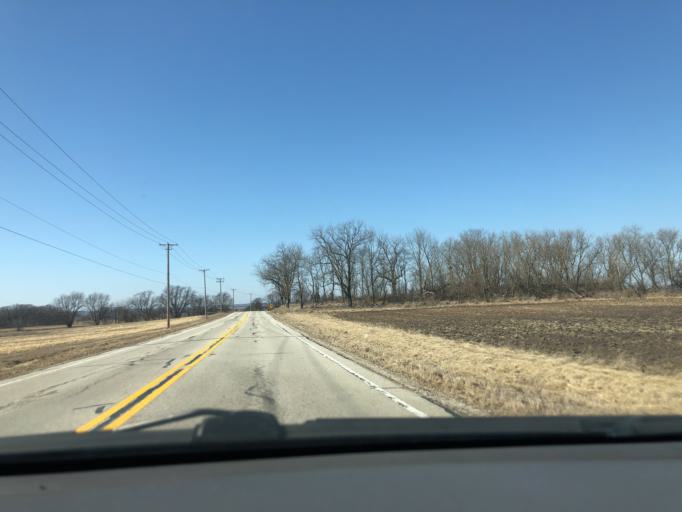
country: US
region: Illinois
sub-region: Kane County
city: Hampshire
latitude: 42.1247
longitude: -88.5057
